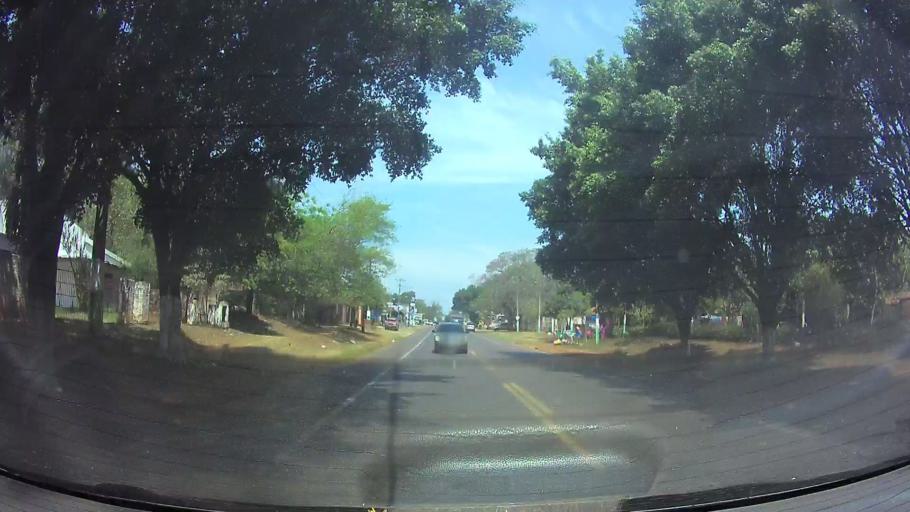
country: PY
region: Central
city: Guarambare
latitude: -25.4228
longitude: -57.4534
